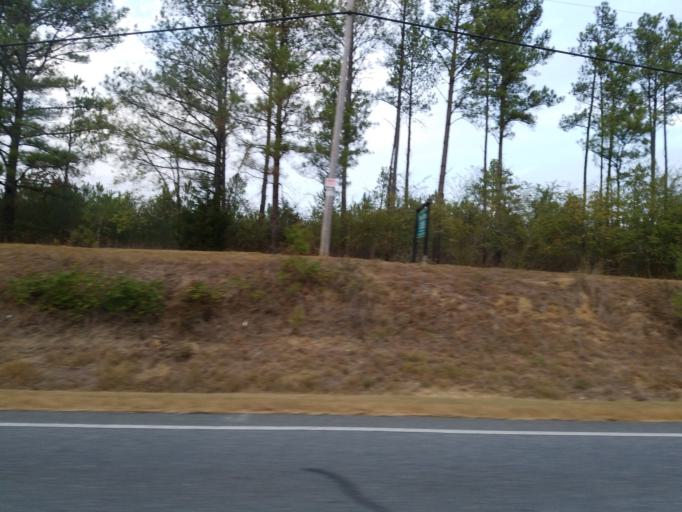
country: US
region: Georgia
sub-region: Murray County
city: Chatsworth
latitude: 34.6064
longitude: -84.8080
